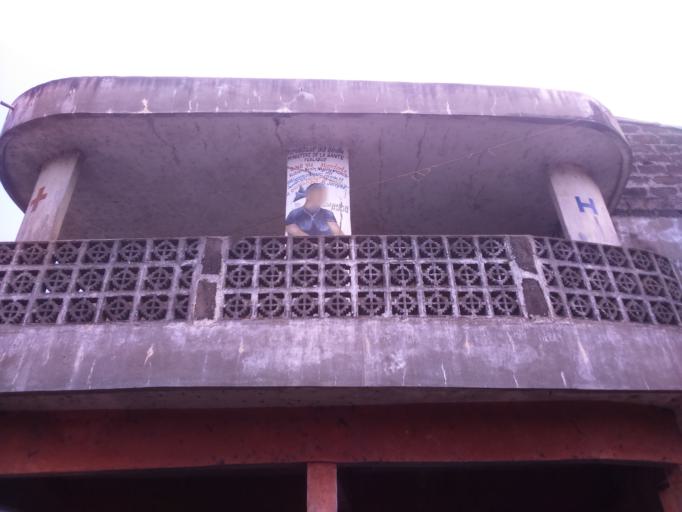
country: BJ
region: Queme
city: Porto-Novo
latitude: 6.5770
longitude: 2.5213
